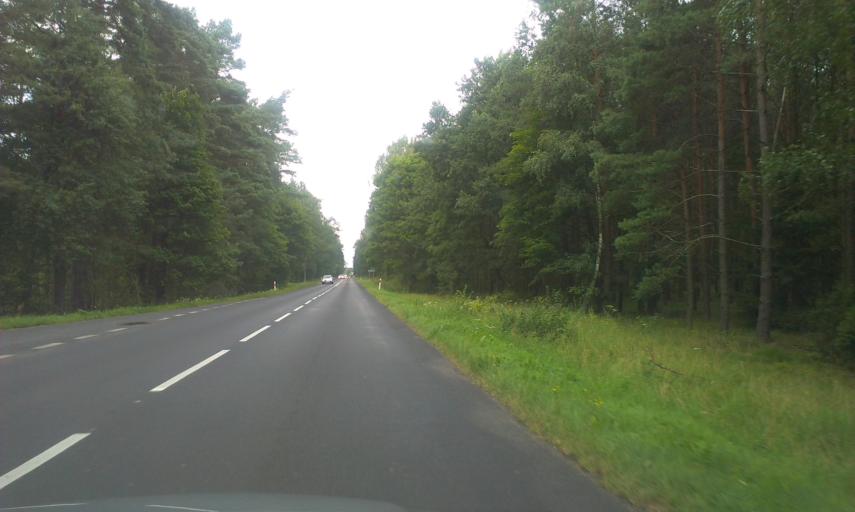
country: PL
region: West Pomeranian Voivodeship
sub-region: Powiat bialogardzki
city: Bialogard
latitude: 53.9687
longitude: 16.0457
